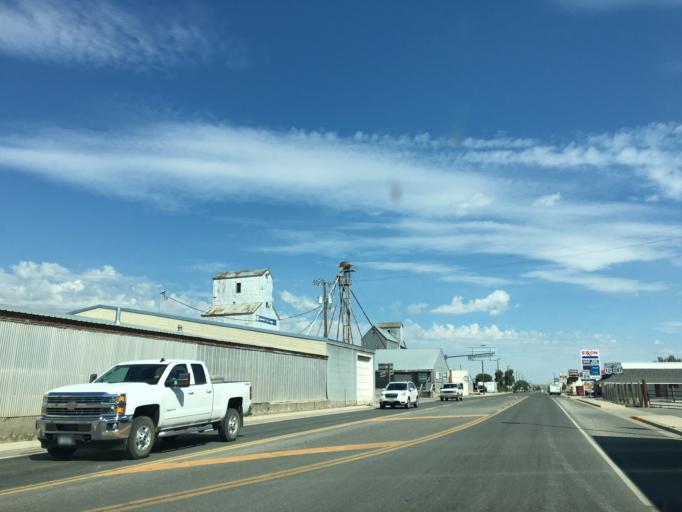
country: US
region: Montana
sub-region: Broadwater County
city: Townsend
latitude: 46.3192
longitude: -111.5214
